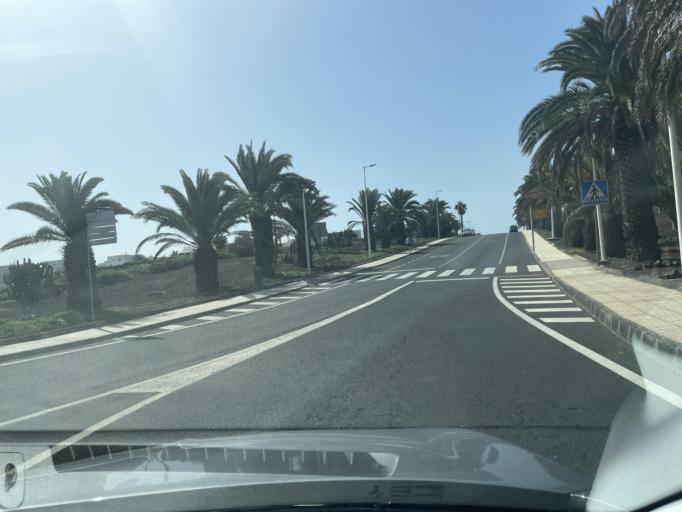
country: ES
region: Canary Islands
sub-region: Provincia de Las Palmas
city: Arrecife
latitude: 28.9981
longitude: -13.4955
